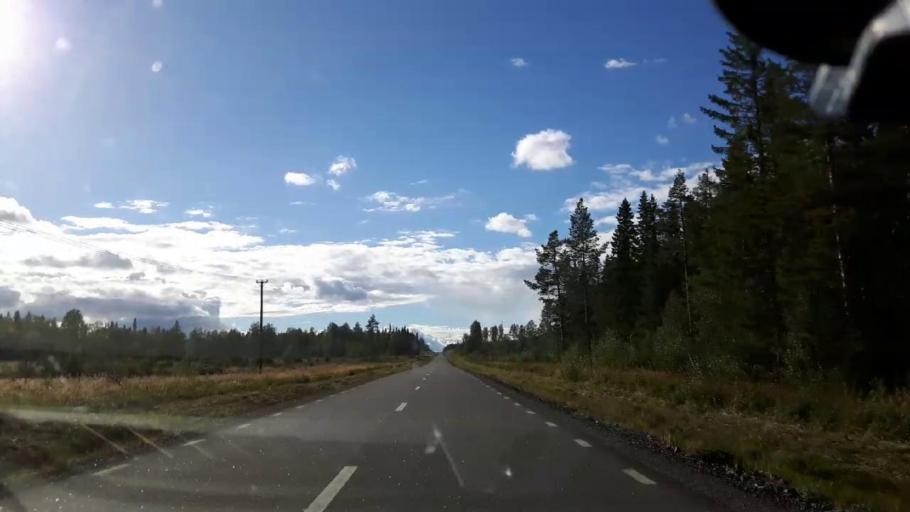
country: SE
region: Jaemtland
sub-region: Stroemsunds Kommun
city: Stroemsund
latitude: 63.5412
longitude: 15.9601
